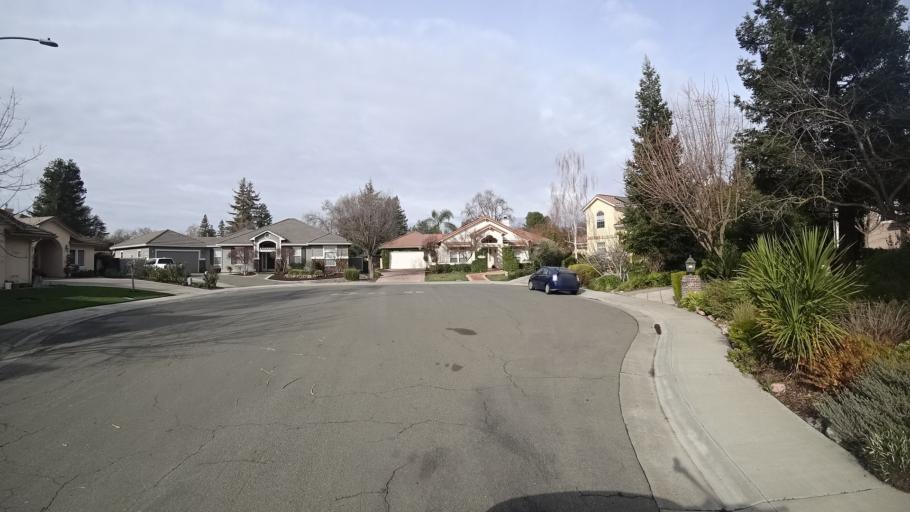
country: US
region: California
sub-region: Yolo County
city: Davis
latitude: 38.5415
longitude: -121.6977
